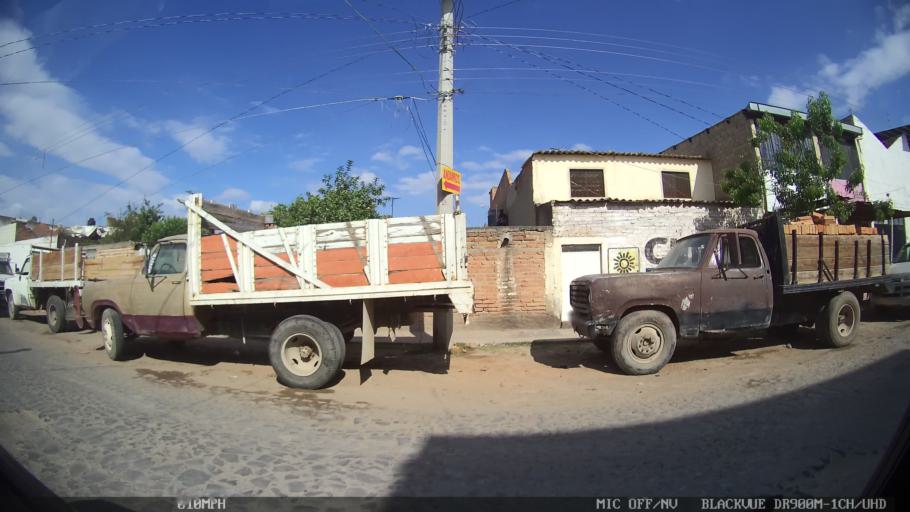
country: MX
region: Jalisco
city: Tonala
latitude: 20.6524
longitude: -103.2515
